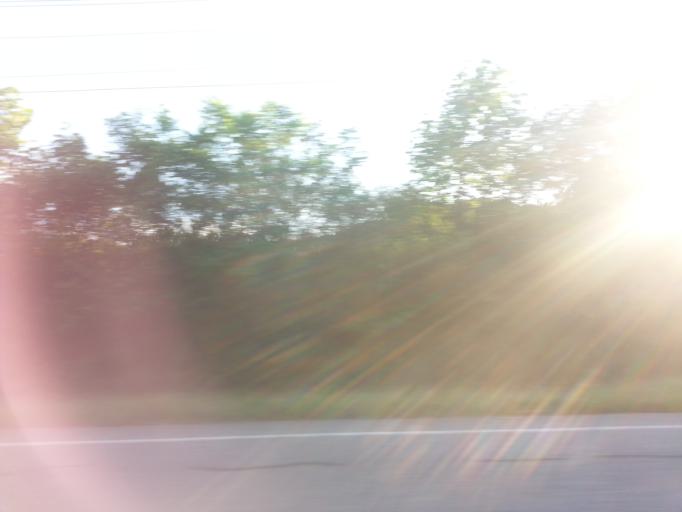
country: US
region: Georgia
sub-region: Union County
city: Blairsville
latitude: 34.9508
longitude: -84.0501
